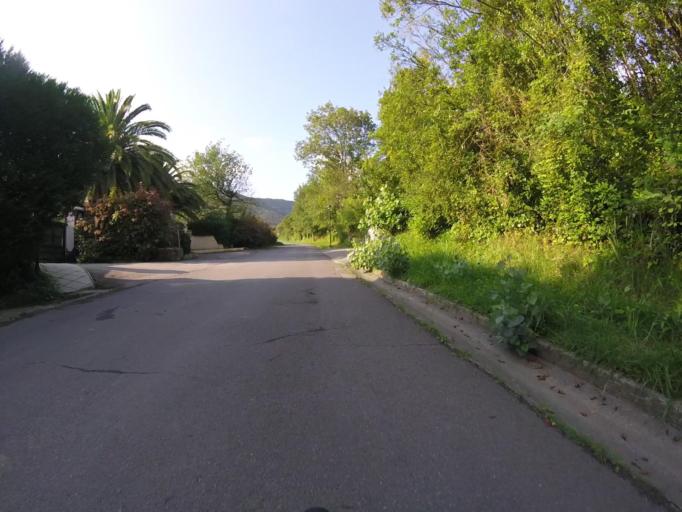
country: ES
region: Basque Country
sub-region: Provincia de Guipuzcoa
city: Irun
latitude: 43.3367
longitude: -1.8338
